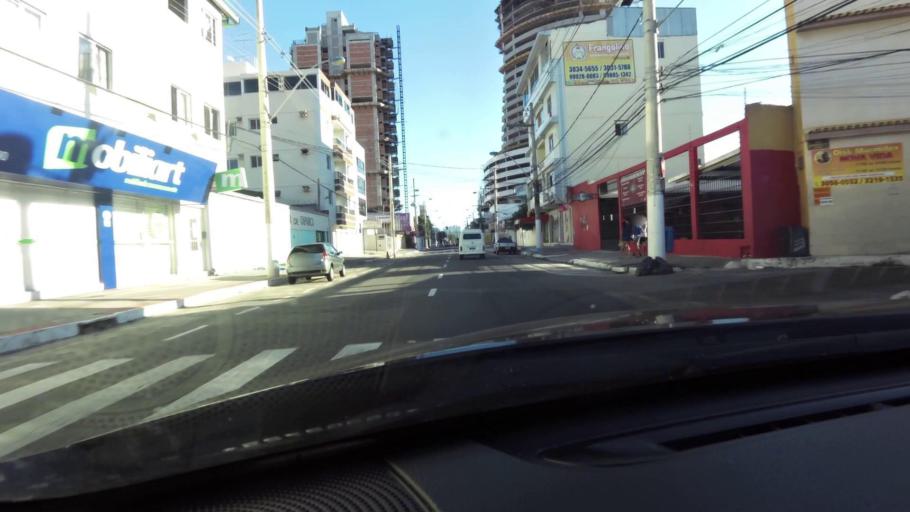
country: BR
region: Espirito Santo
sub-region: Vila Velha
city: Vila Velha
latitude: -20.3578
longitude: -40.2970
